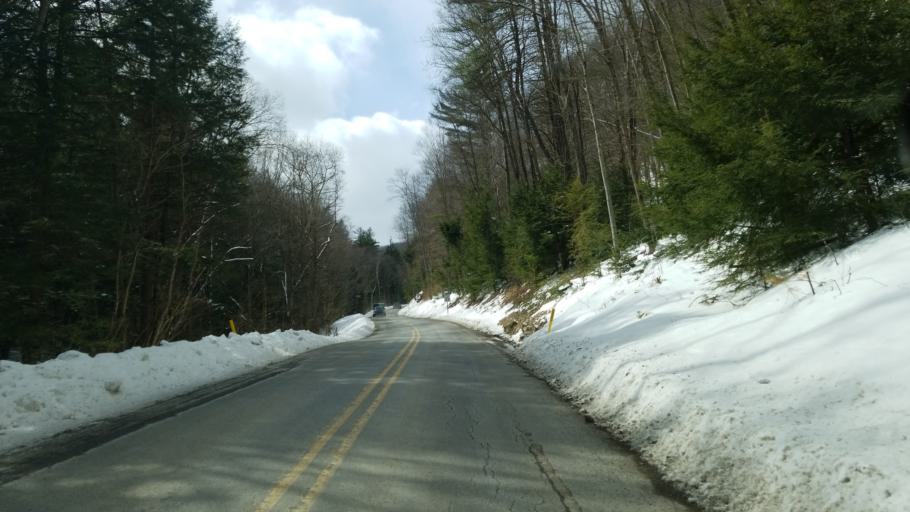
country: US
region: Pennsylvania
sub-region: Clearfield County
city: Shiloh
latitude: 41.2465
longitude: -78.1632
